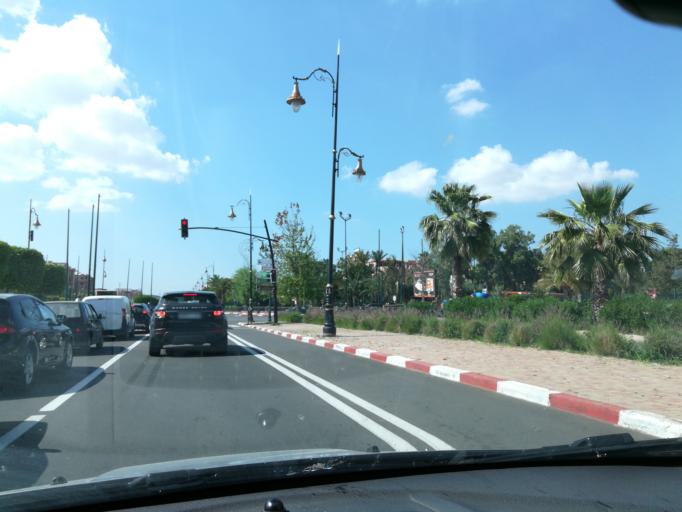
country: MA
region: Marrakech-Tensift-Al Haouz
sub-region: Marrakech
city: Marrakesh
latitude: 31.6173
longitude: -8.0075
